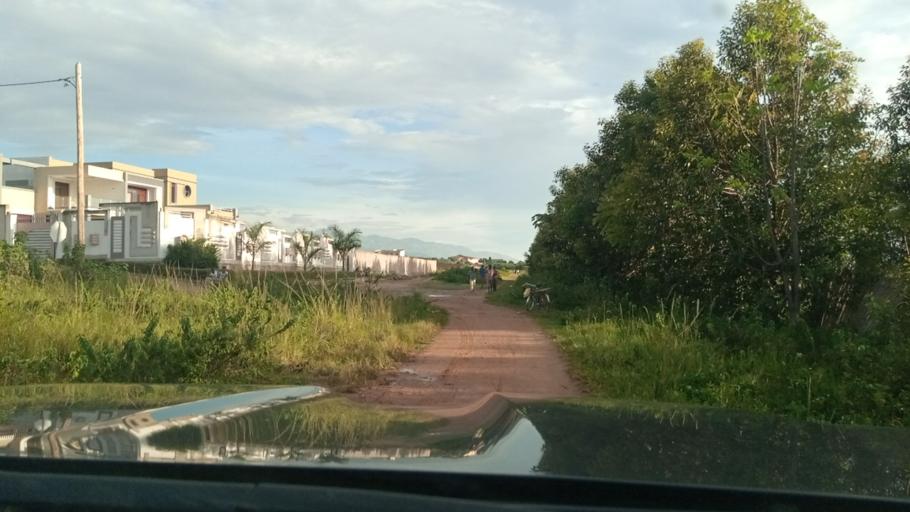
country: BI
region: Bujumbura Mairie
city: Bujumbura
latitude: -3.4467
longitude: 29.3455
